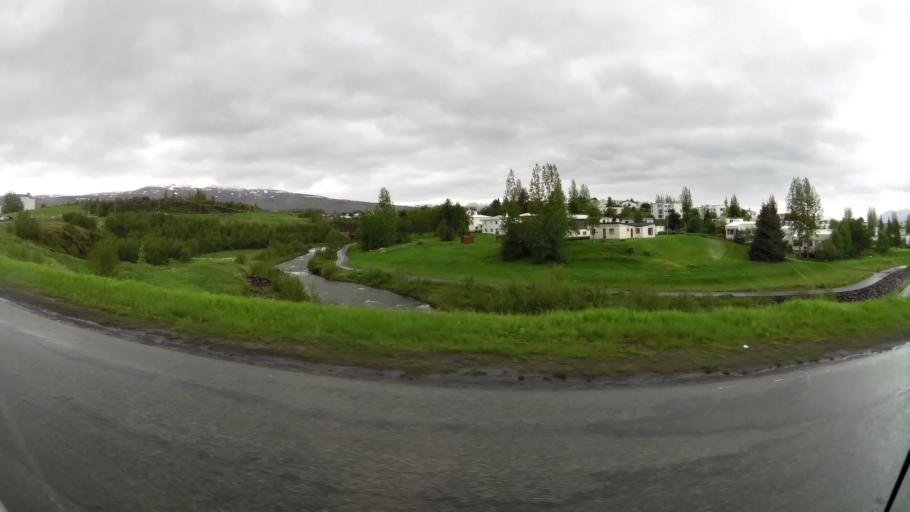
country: IS
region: Northeast
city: Akureyri
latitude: 65.6861
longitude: -18.1101
